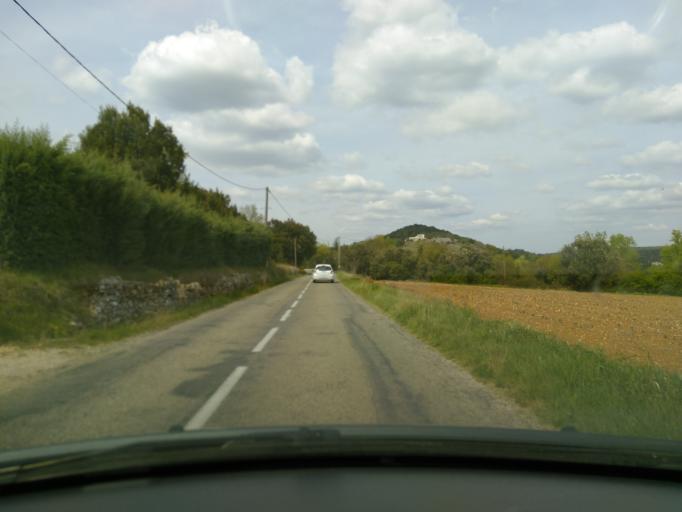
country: FR
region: Rhone-Alpes
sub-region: Departement de l'Ardeche
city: Ruoms
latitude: 44.4282
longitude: 4.4158
